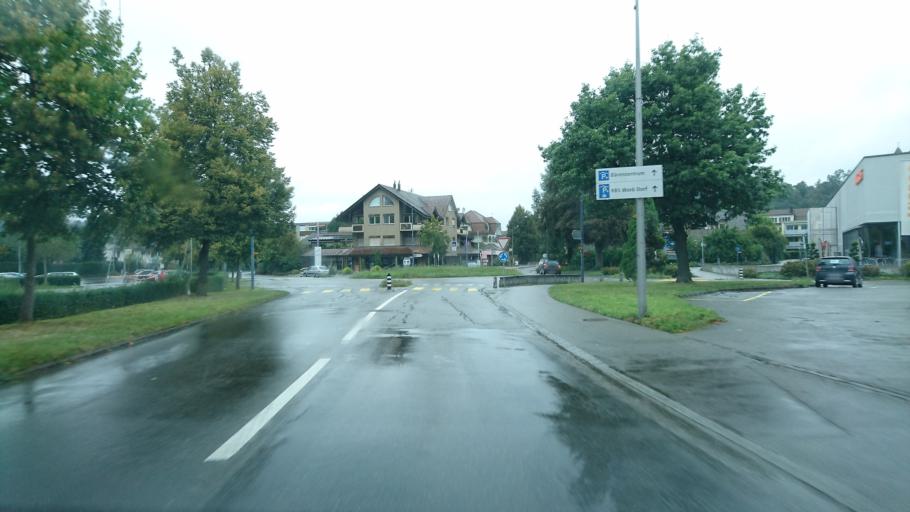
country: CH
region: Bern
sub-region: Bern-Mittelland District
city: Worb
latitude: 46.9259
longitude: 7.5645
